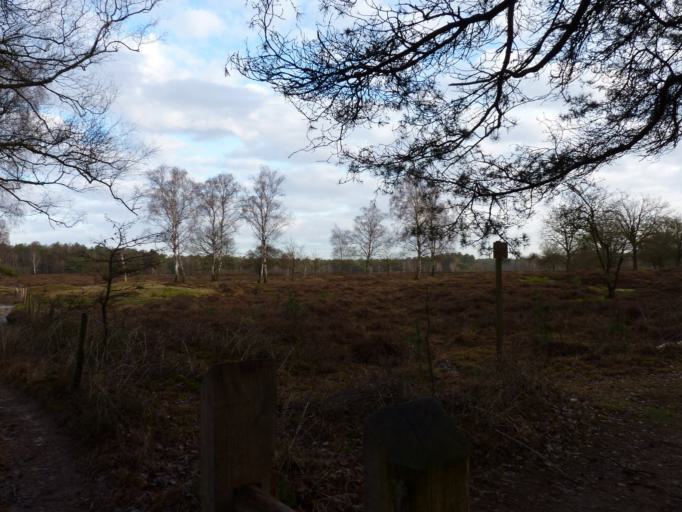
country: NL
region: Utrecht
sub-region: Gemeente Soest
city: Soest
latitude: 52.1850
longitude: 5.2406
